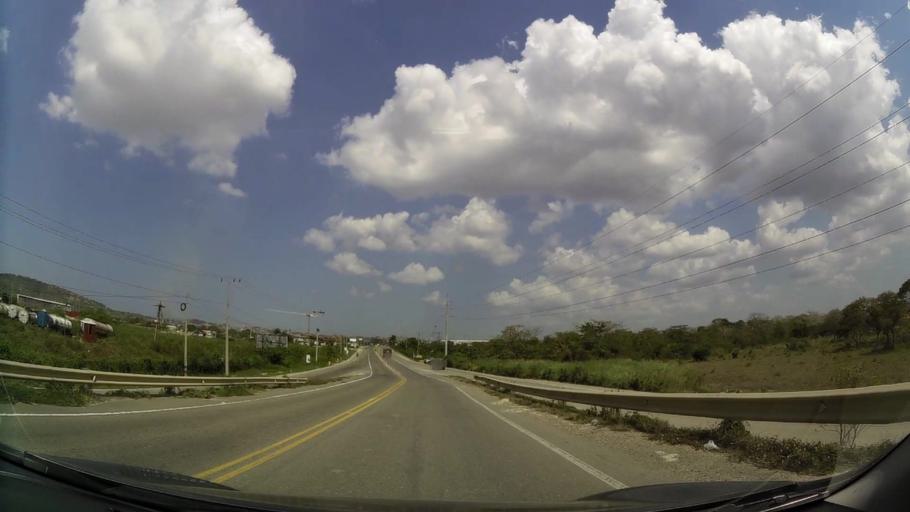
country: CO
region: Bolivar
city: Cartagena
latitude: 10.3445
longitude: -75.4842
